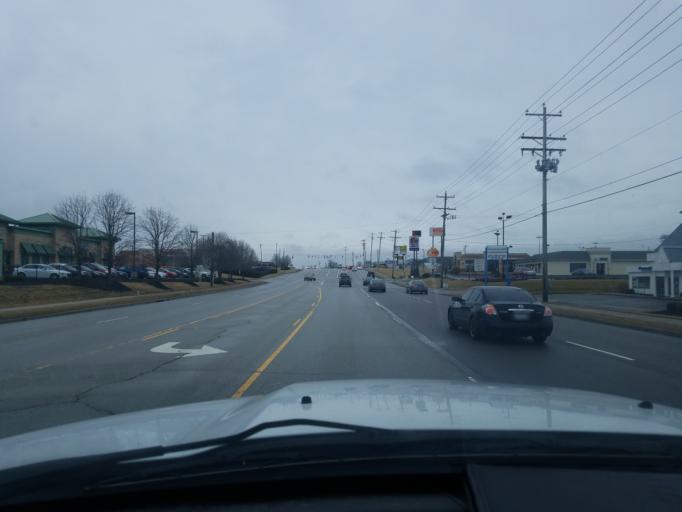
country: US
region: Ohio
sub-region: Butler County
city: Wetherington
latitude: 39.3535
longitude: -84.3678
